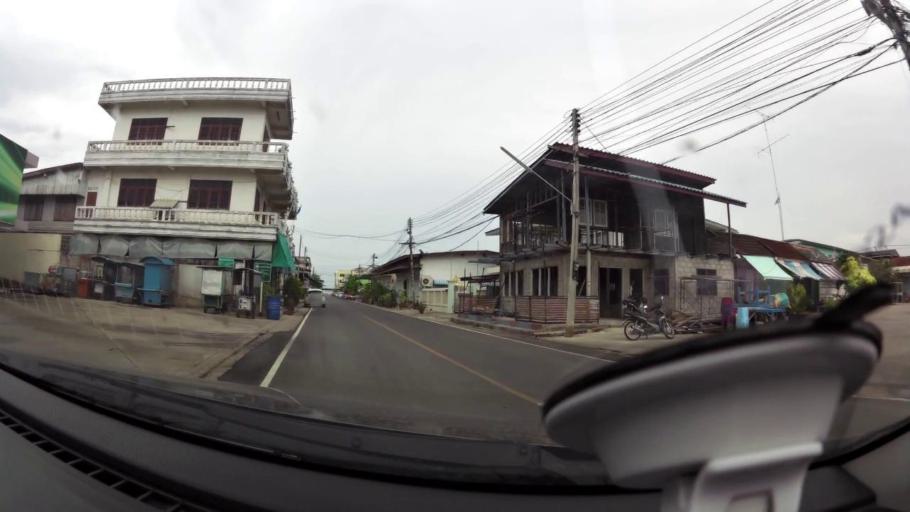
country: TH
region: Prachuap Khiri Khan
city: Pran Buri
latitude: 12.4024
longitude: 99.9919
